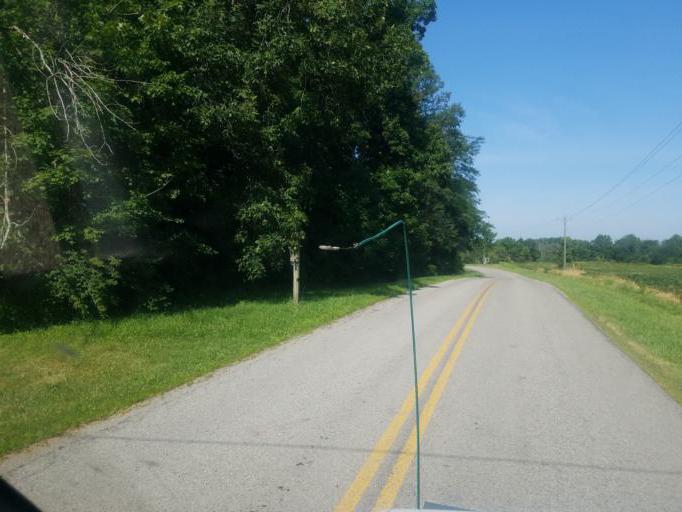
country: US
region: Ohio
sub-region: Union County
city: Marysville
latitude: 40.2847
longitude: -83.2871
